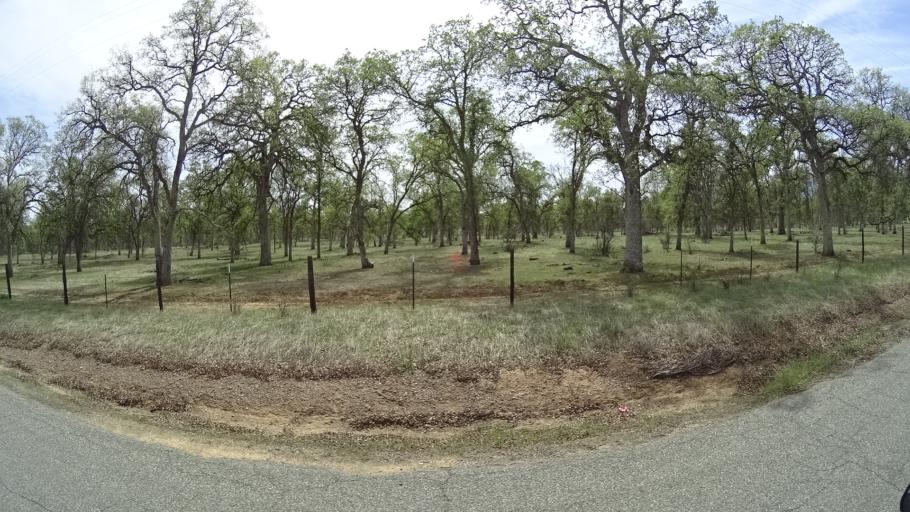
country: US
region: California
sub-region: Glenn County
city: Willows
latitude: 39.5916
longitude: -122.5653
